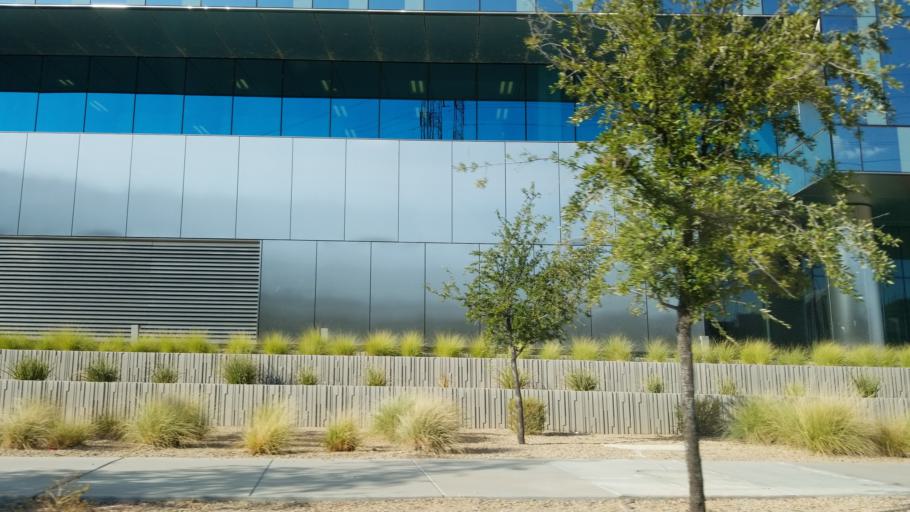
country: US
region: Arizona
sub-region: Maricopa County
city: Tempe Junction
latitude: 33.4296
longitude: -111.9321
